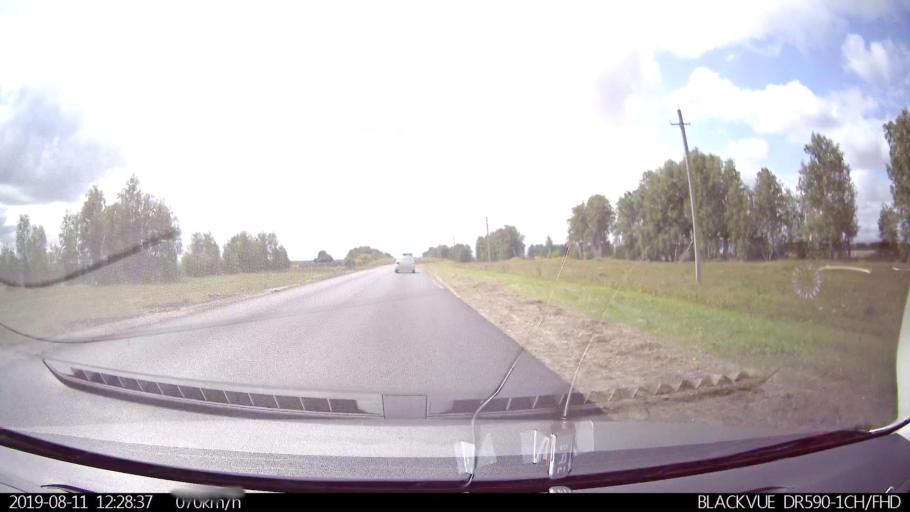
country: RU
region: Ulyanovsk
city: Ignatovka
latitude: 53.8422
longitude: 47.9102
